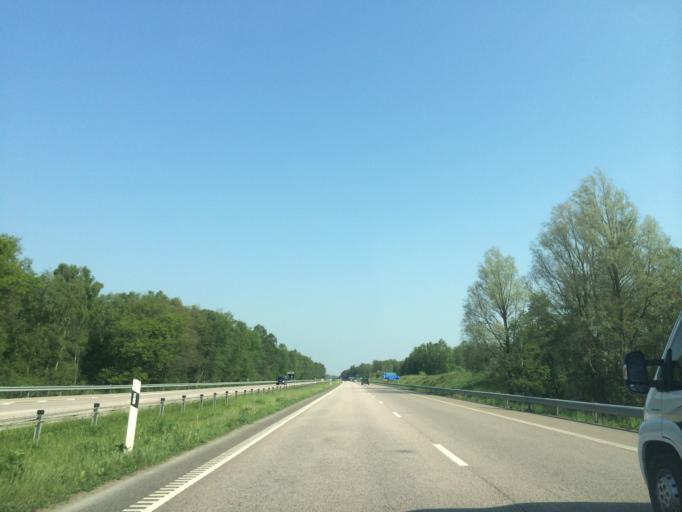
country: SE
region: Skane
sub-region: Helsingborg
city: Barslov
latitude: 56.0509
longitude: 12.7849
